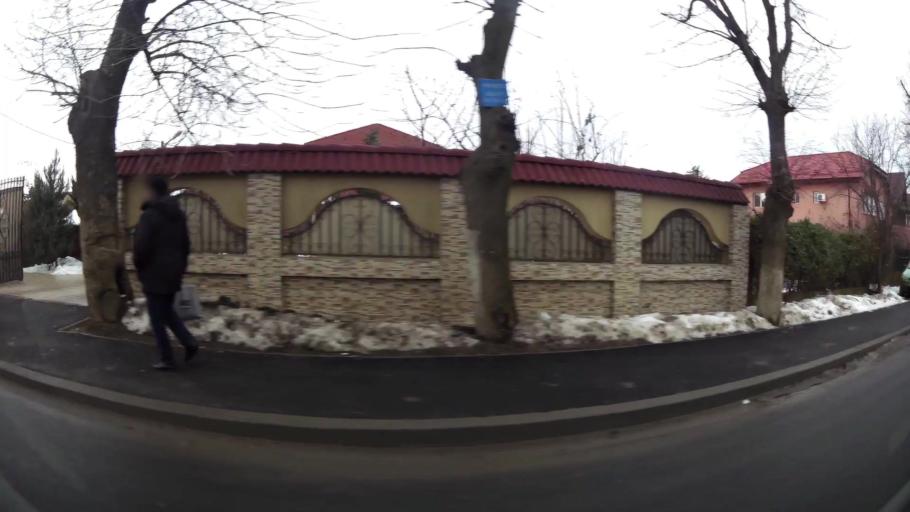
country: RO
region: Ilfov
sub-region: Comuna Pantelimon
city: Pantelimon
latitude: 44.4609
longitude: 26.2110
